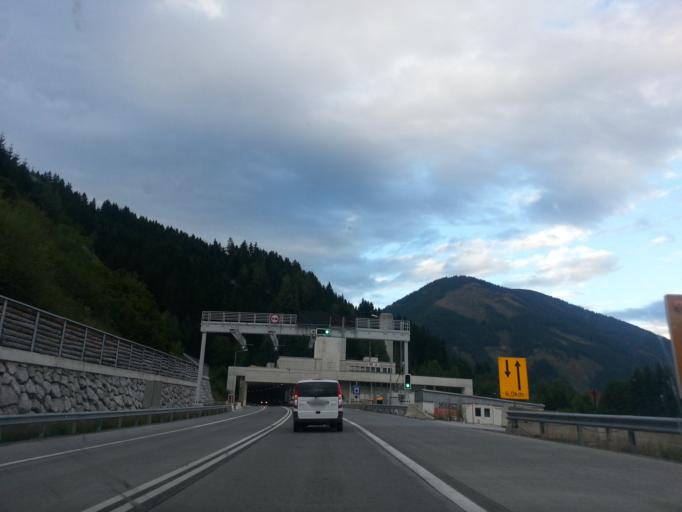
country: AT
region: Styria
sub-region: Politischer Bezirk Liezen
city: Ardning
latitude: 47.5891
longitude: 14.3456
